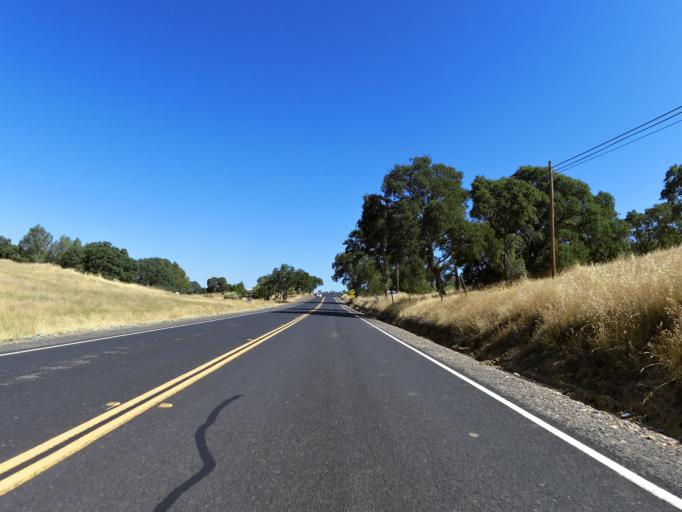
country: US
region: California
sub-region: Tuolumne County
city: Jamestown
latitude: 37.6921
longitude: -120.3316
